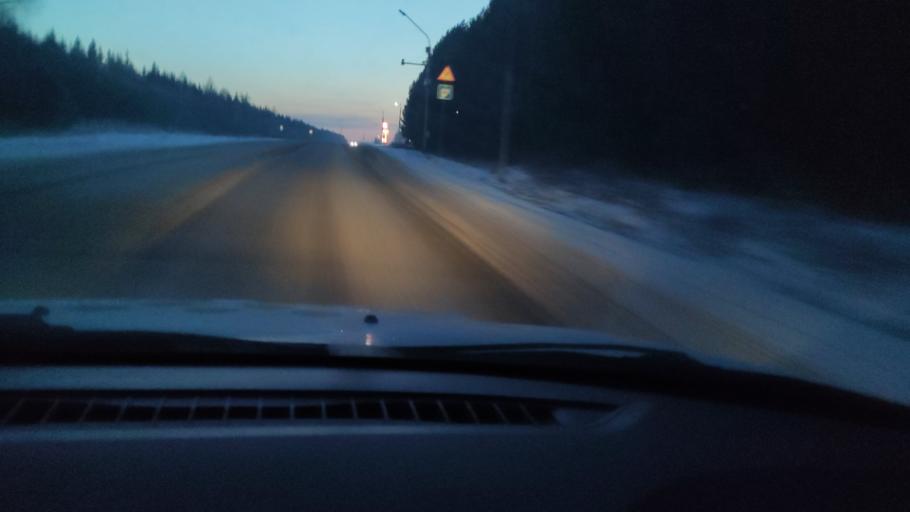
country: RU
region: Perm
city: Kungur
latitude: 57.4113
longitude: 56.9091
